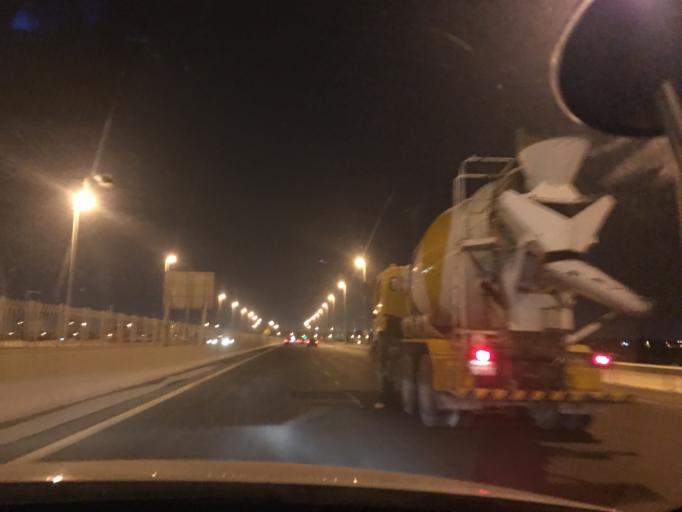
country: BH
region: Muharraq
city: Al Muharraq
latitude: 26.2925
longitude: 50.6406
